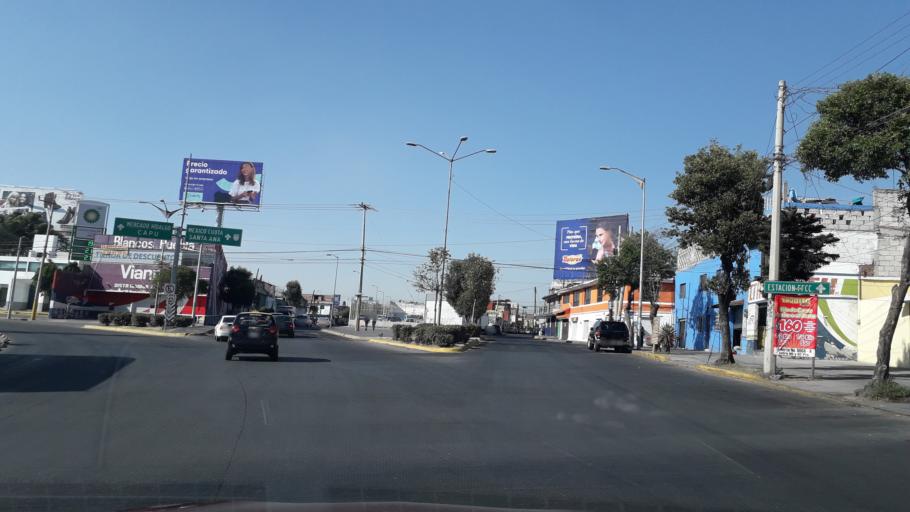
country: MX
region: Puebla
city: Puebla
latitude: 19.0701
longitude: -98.1913
